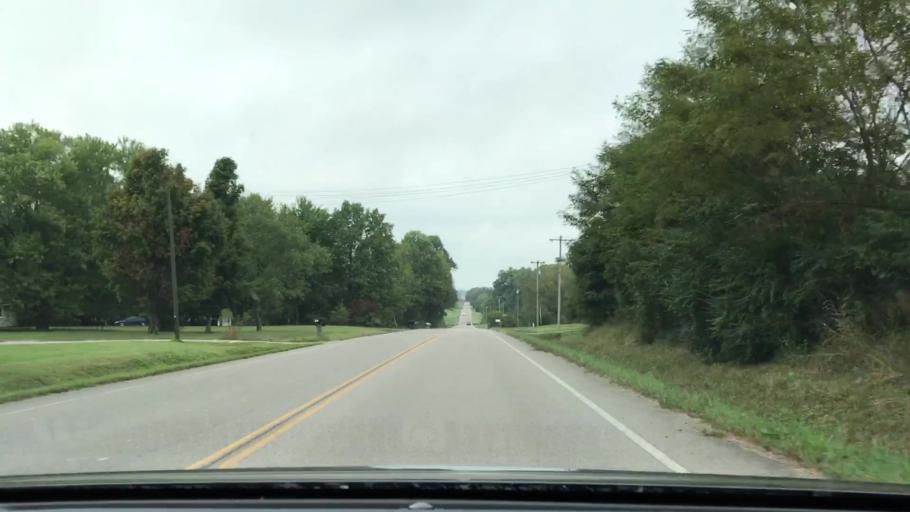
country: US
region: Tennessee
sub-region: Sumner County
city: Portland
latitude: 36.5179
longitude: -86.5009
